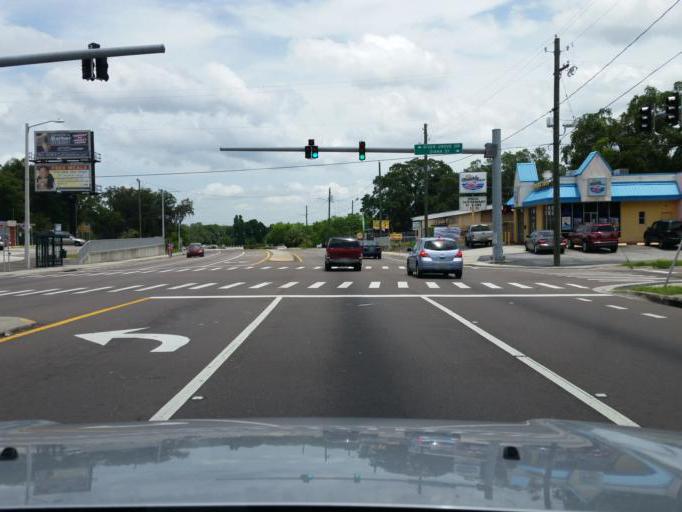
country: US
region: Florida
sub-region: Hillsborough County
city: Temple Terrace
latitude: 28.0068
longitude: -82.4141
